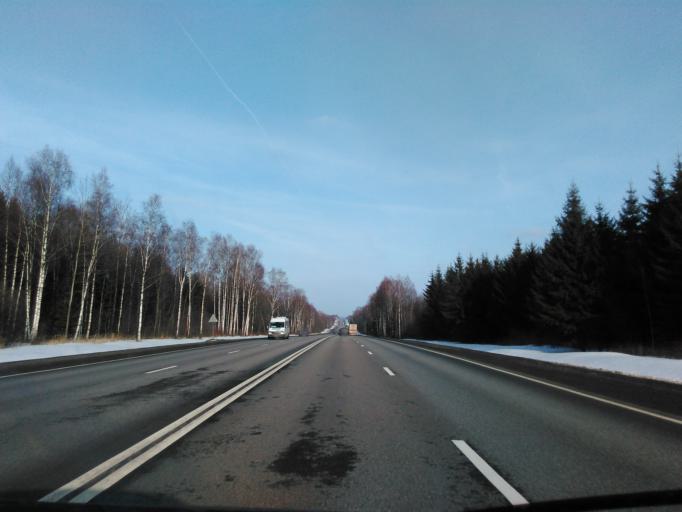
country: RU
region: Smolensk
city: Vyaz'ma
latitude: 55.1879
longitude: 34.0639
